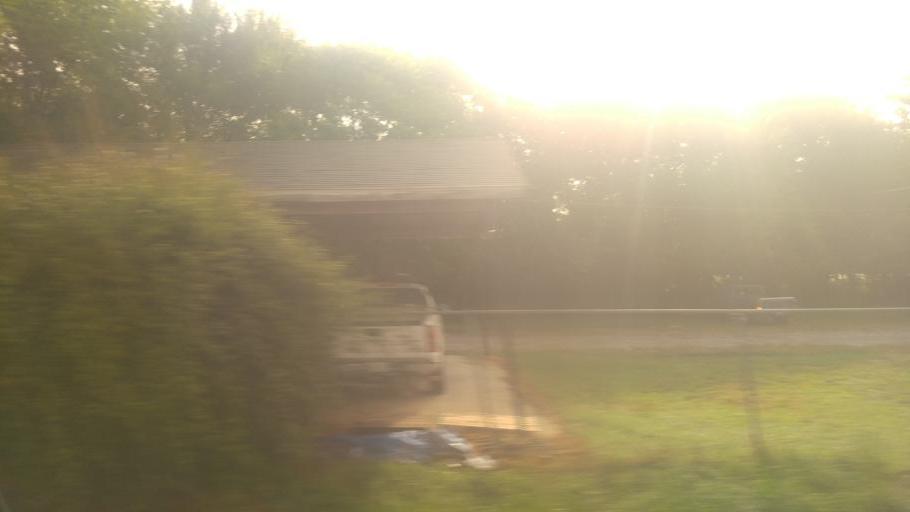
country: US
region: North Carolina
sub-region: Wake County
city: Raleigh
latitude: 35.7621
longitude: -78.6368
